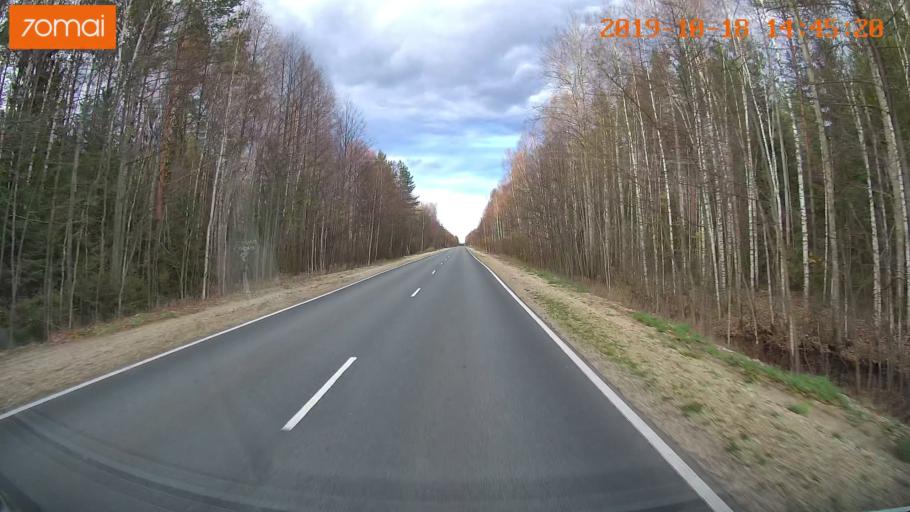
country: RU
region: Vladimir
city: Velikodvorskiy
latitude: 55.3532
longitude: 40.6787
